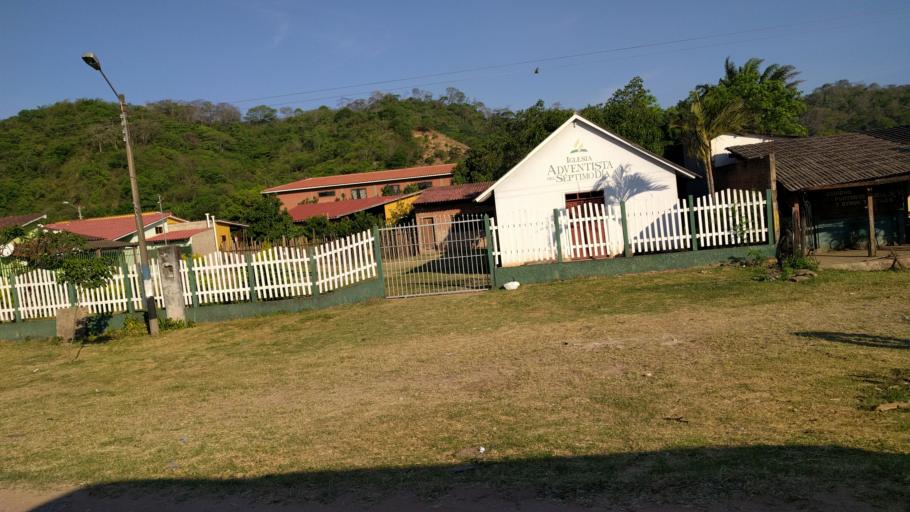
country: BO
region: Santa Cruz
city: Jorochito
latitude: -18.0598
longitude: -63.4312
